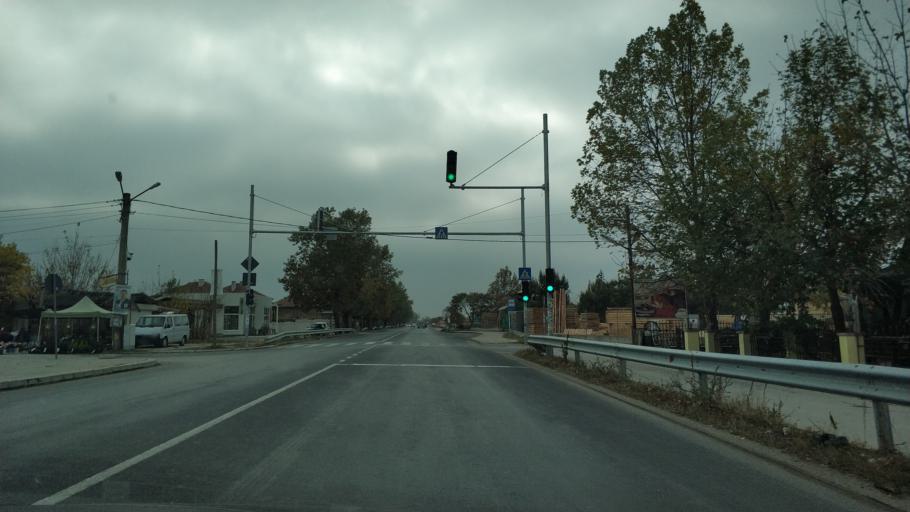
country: BG
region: Plovdiv
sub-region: Obshtina Kaloyanovo
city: Kaloyanovo
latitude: 42.2841
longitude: 24.7338
